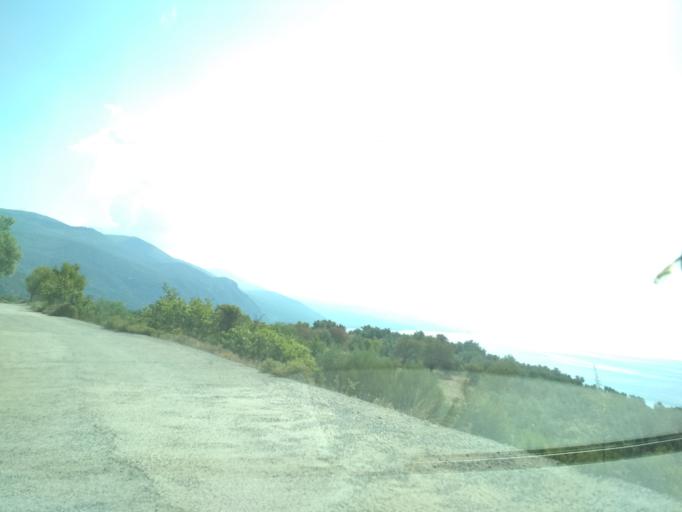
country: GR
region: Central Greece
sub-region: Nomos Evvoias
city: Oreoi
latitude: 38.8521
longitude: 23.1100
